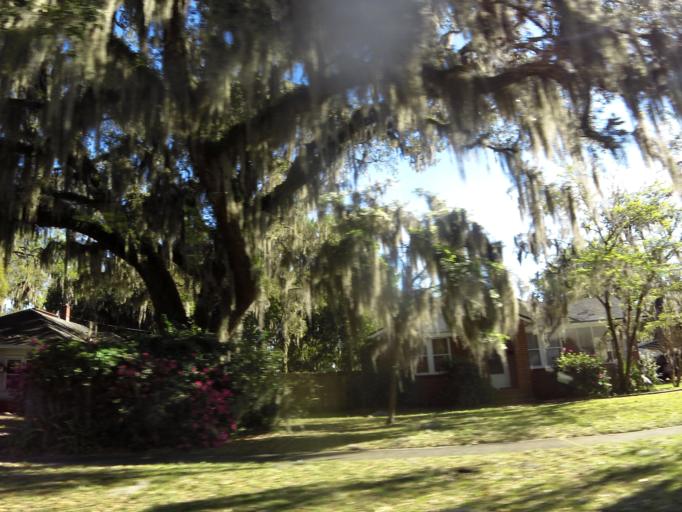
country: US
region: Florida
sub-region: Duval County
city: Jacksonville
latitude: 30.3794
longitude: -81.6480
